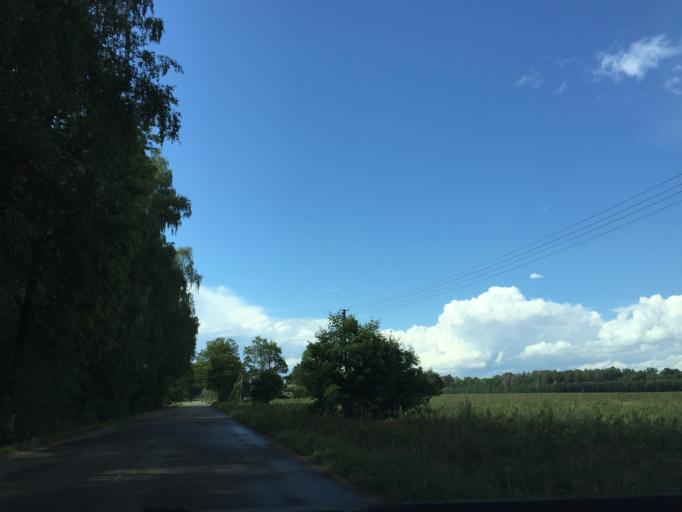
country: LT
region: Siauliu apskritis
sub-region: Joniskis
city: Joniskis
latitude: 56.3288
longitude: 23.5724
